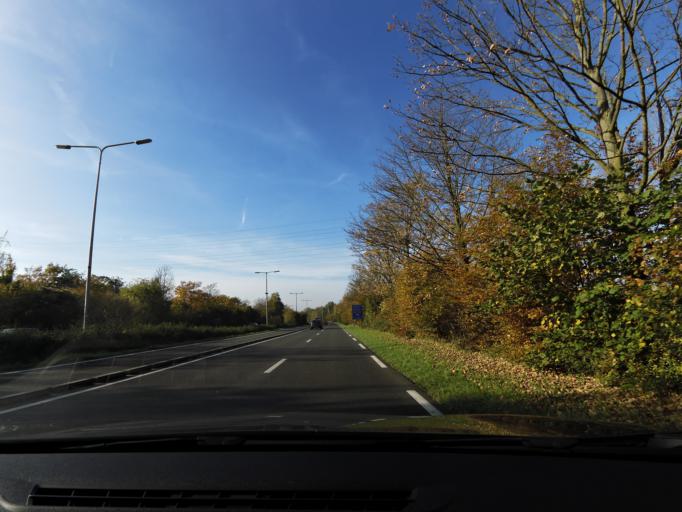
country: NL
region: South Holland
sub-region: Gemeente Ridderkerk
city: Ridderkerk
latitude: 51.8845
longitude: 4.5862
